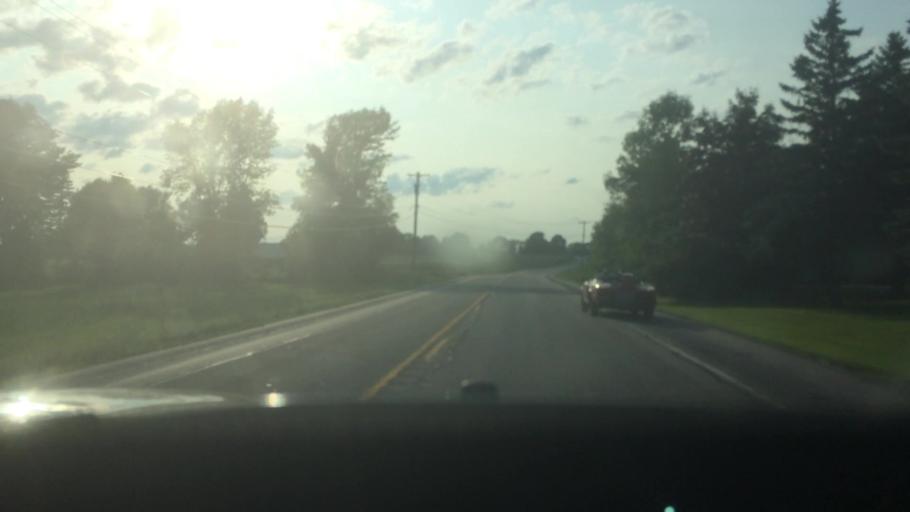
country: US
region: New York
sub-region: St. Lawrence County
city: Ogdensburg
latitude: 44.6688
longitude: -75.3769
